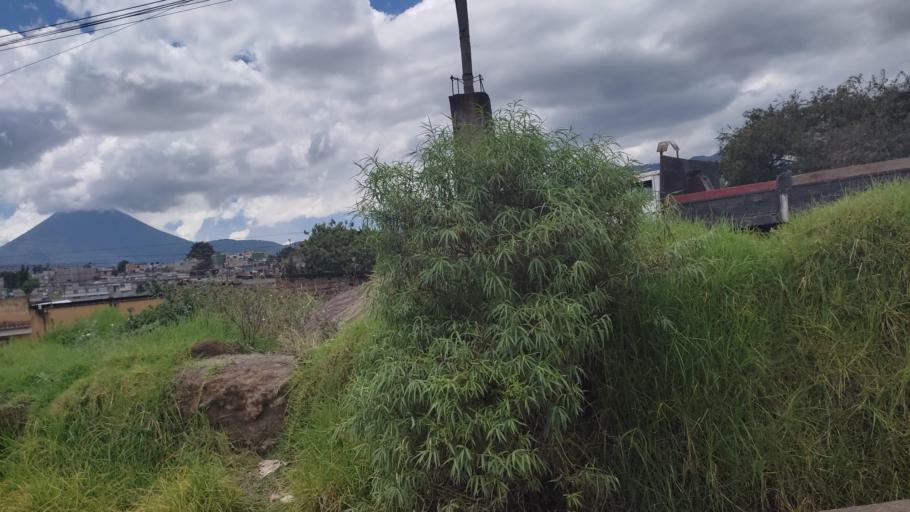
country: GT
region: Quetzaltenango
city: Quetzaltenango
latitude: 14.8571
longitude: -91.5262
